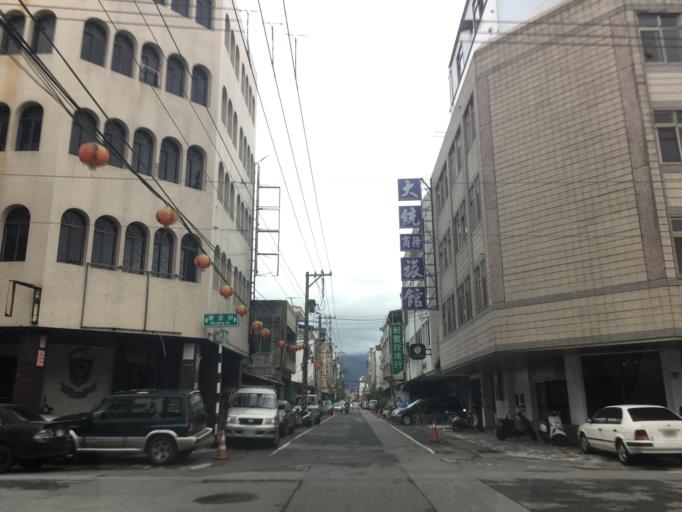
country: TW
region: Taiwan
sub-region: Hualien
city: Hualian
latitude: 23.9740
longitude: 121.6056
